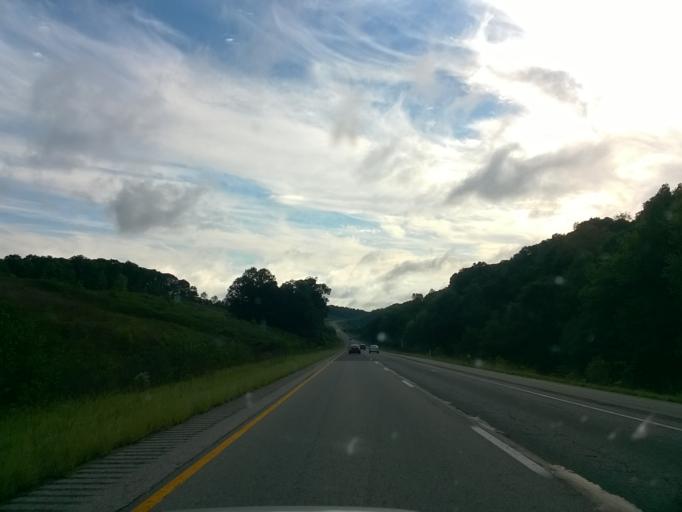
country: US
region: Indiana
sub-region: Dubois County
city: Ferdinand
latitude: 38.2053
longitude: -86.8071
